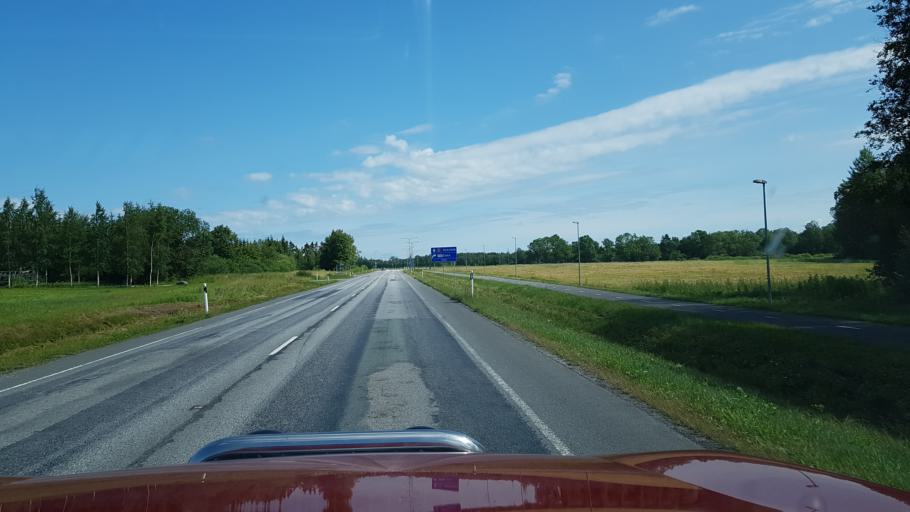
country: EE
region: Jaervamaa
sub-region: Paide linn
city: Paide
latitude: 58.9365
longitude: 25.6362
